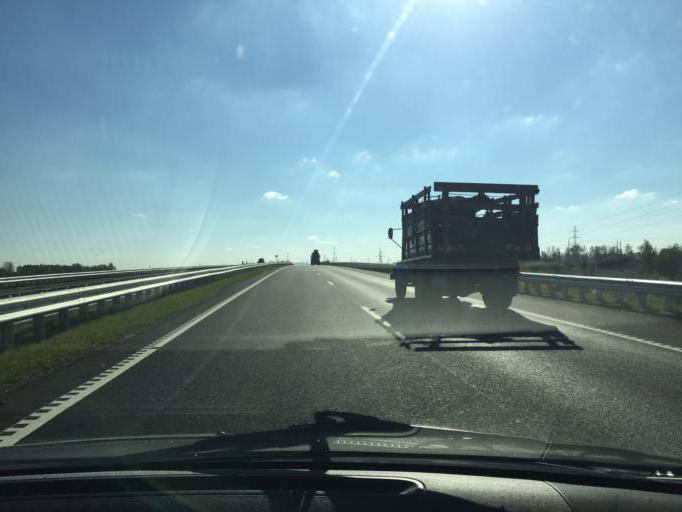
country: BY
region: Minsk
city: Slutsk
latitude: 53.0145
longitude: 27.4858
